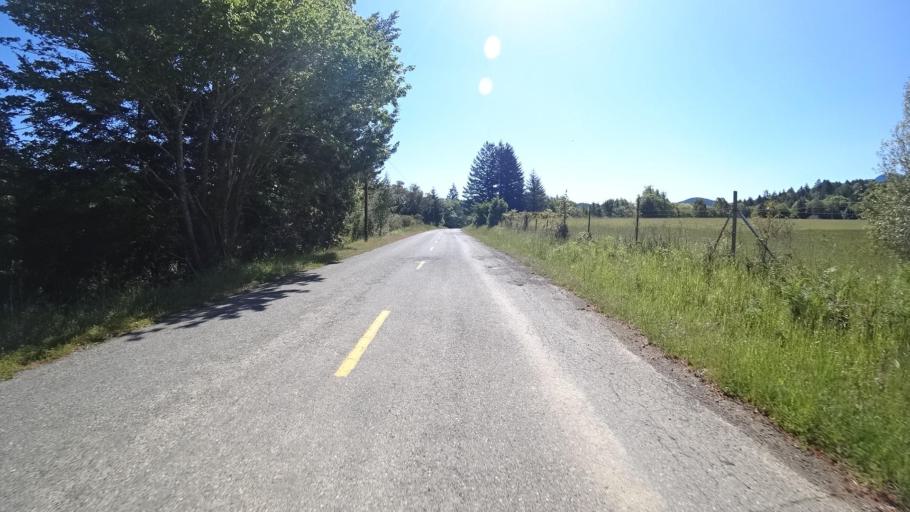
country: US
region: California
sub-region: Humboldt County
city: Rio Dell
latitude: 40.2491
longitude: -124.1716
